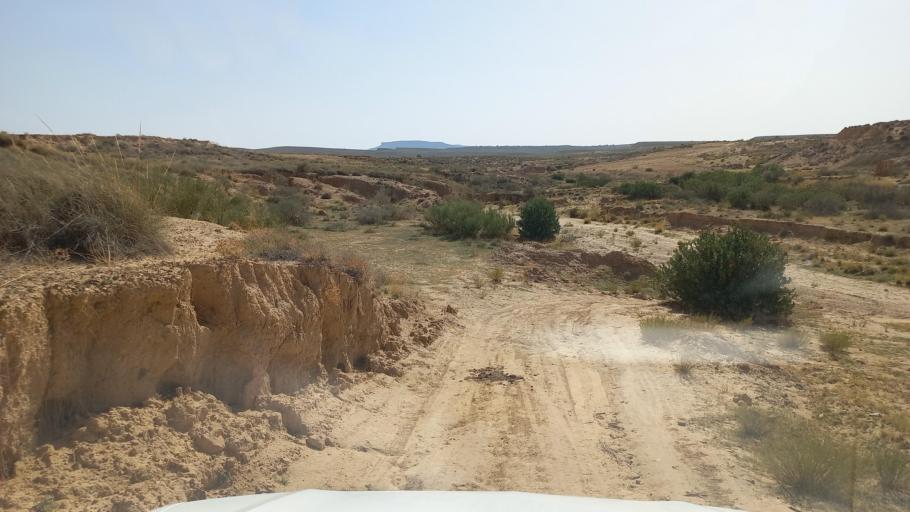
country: TN
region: Al Qasrayn
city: Kasserine
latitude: 35.2158
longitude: 9.0182
